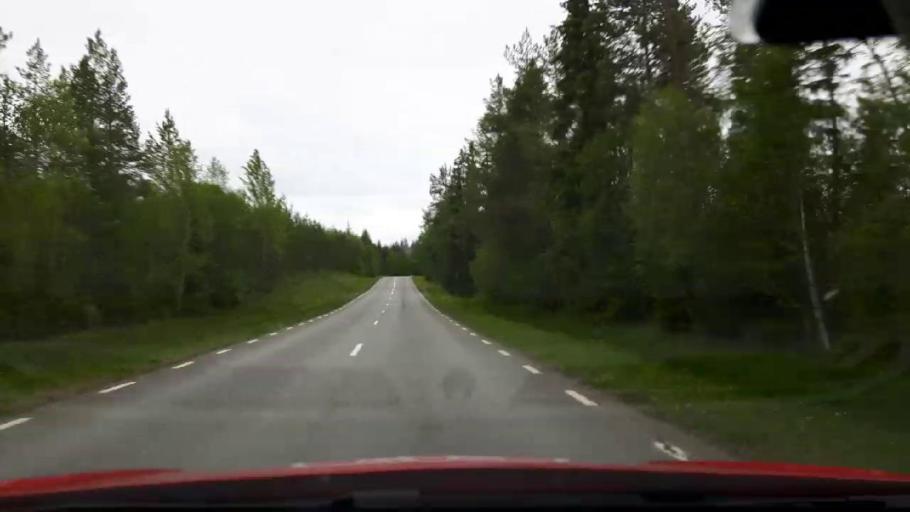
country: SE
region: Jaemtland
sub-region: Stroemsunds Kommun
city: Stroemsund
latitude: 63.4819
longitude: 15.4447
